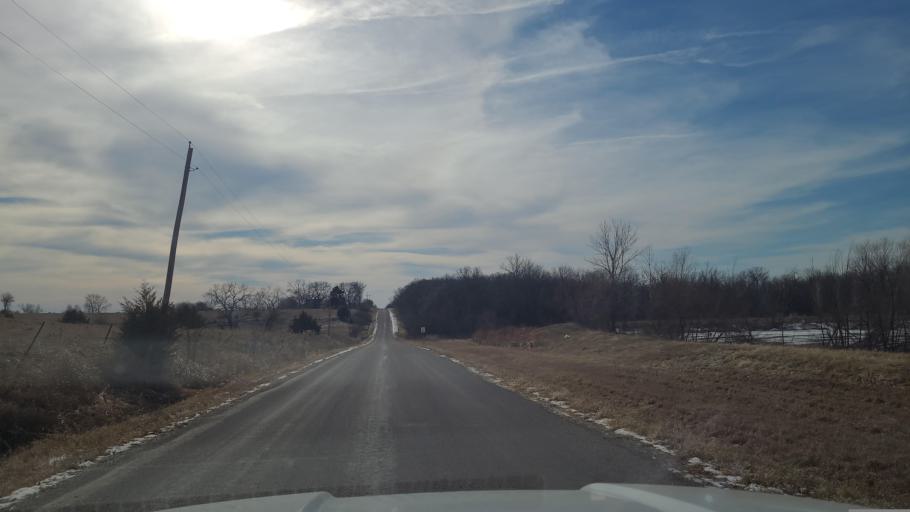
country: US
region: Kansas
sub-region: Douglas County
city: Lawrence
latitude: 38.8985
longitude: -95.1863
